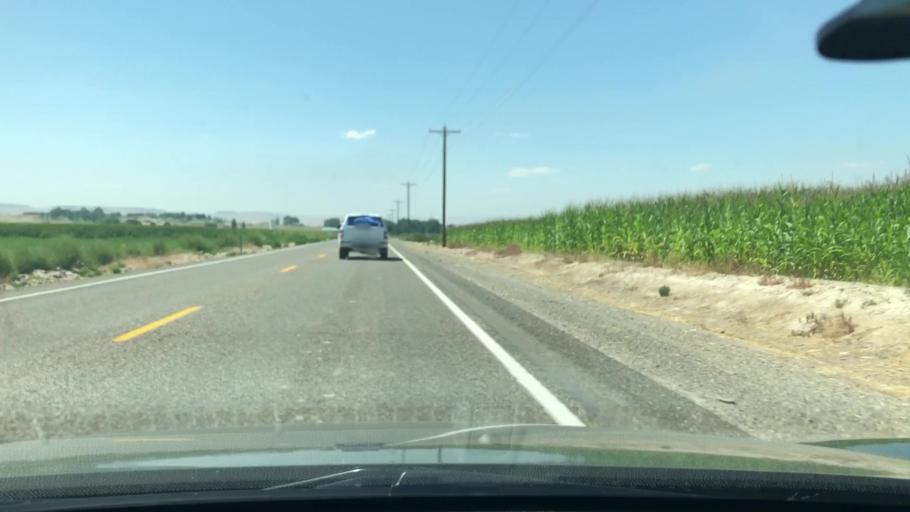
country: US
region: Idaho
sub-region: Owyhee County
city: Marsing
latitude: 43.5453
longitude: -116.8794
